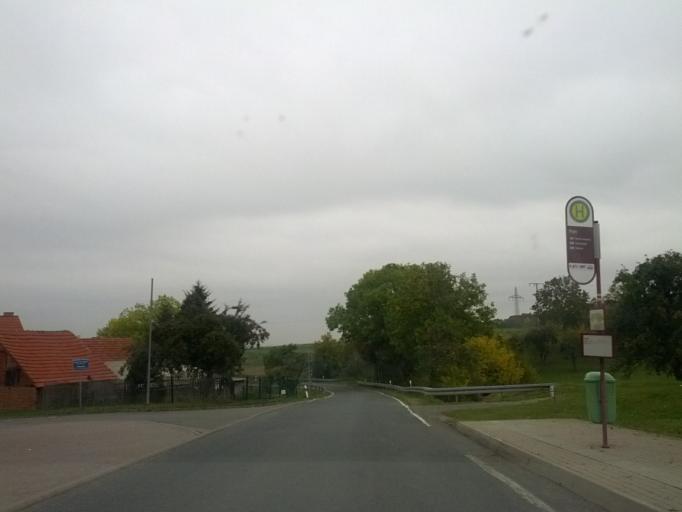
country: DE
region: Thuringia
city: Klettbach
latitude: 50.9325
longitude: 11.1647
